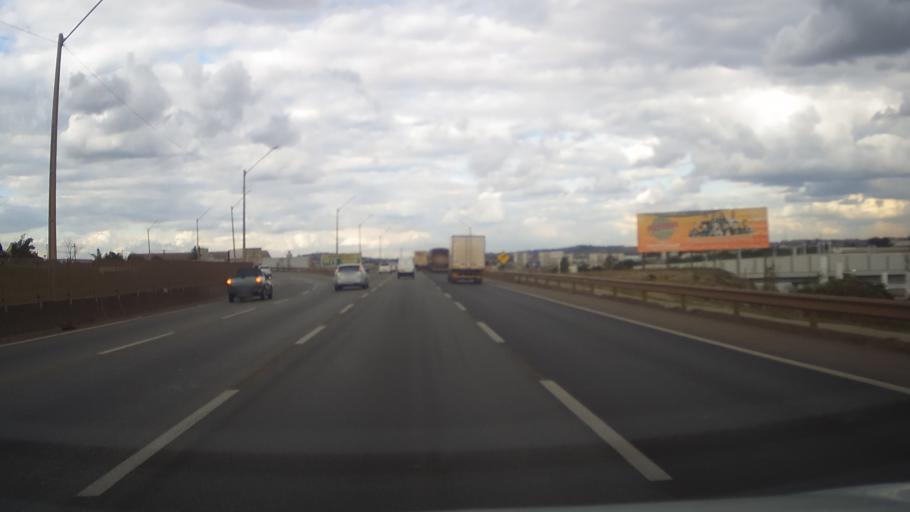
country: BR
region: Minas Gerais
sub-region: Betim
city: Betim
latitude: -19.9579
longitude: -44.1505
